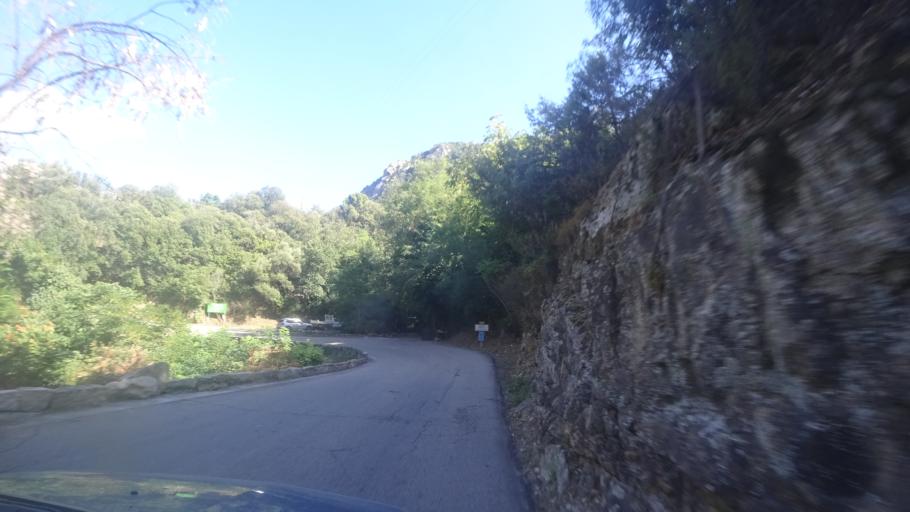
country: FR
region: Corsica
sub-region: Departement de la Corse-du-Sud
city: Cargese
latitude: 42.2620
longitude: 8.7074
